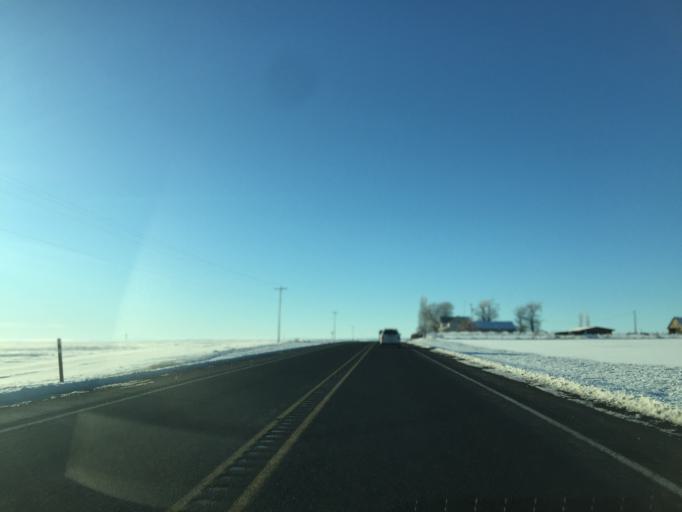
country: US
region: Washington
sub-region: Okanogan County
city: Coulee Dam
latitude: 47.6844
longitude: -119.0163
